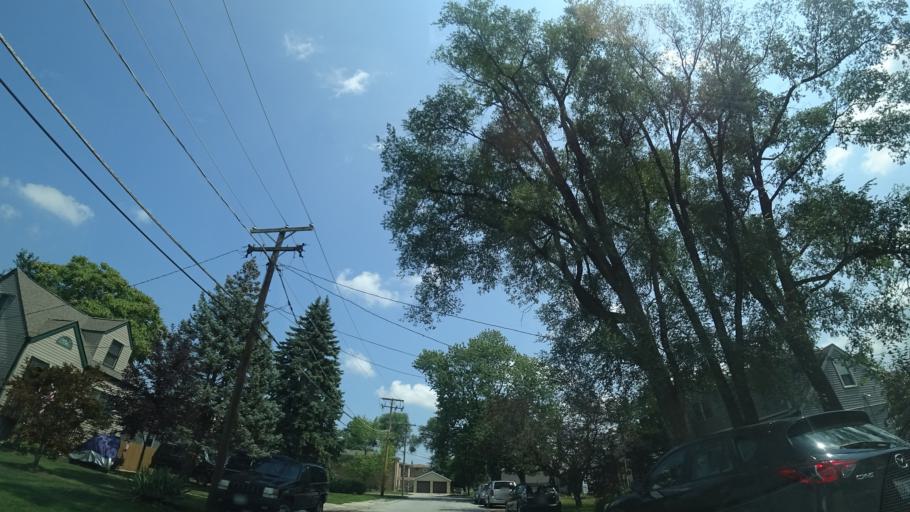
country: US
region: Illinois
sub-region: Cook County
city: Worth
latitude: 41.6911
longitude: -87.7894
